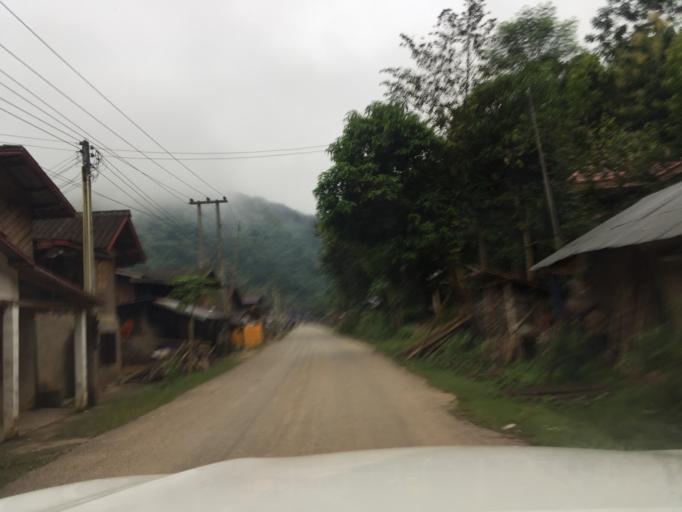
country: LA
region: Phongsali
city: Khoa
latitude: 21.0699
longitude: 102.3776
